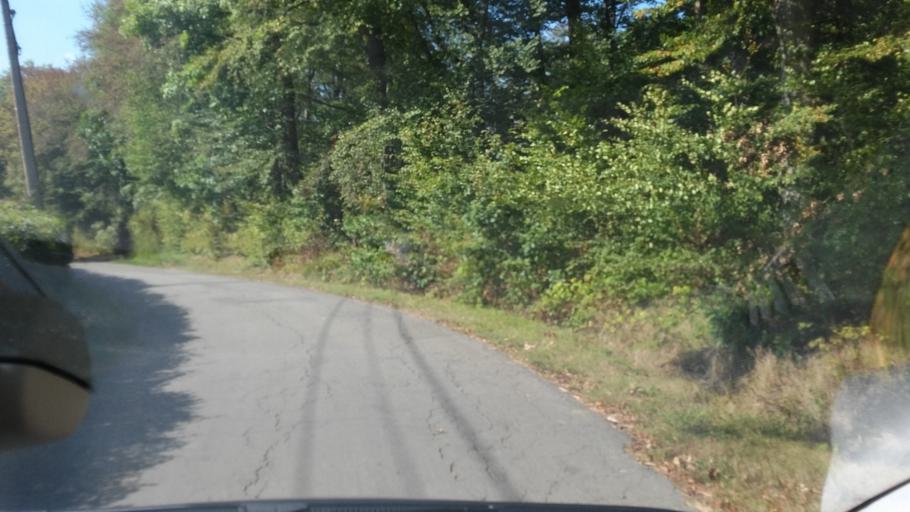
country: LU
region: Diekirch
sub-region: Canton de Redange
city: Beckerich
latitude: 49.7115
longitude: 5.8693
